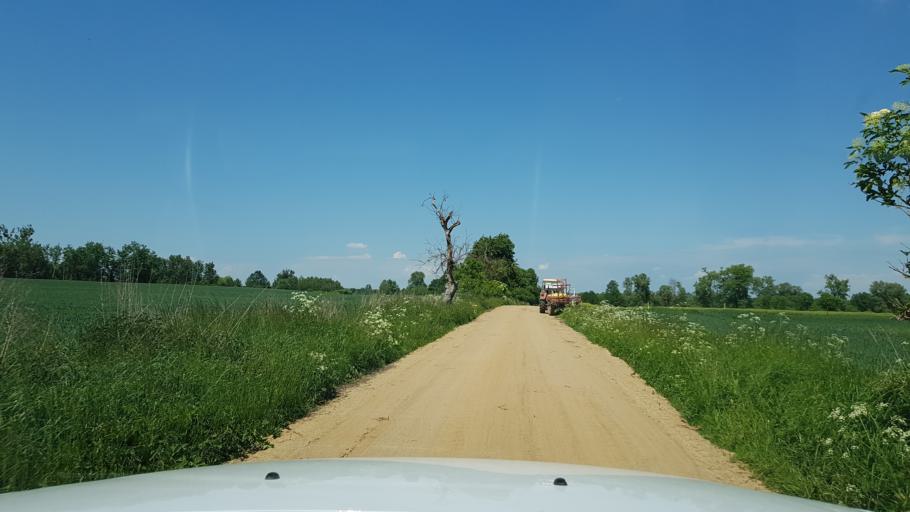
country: PL
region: West Pomeranian Voivodeship
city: Trzcinsko Zdroj
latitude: 52.9481
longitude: 14.5811
